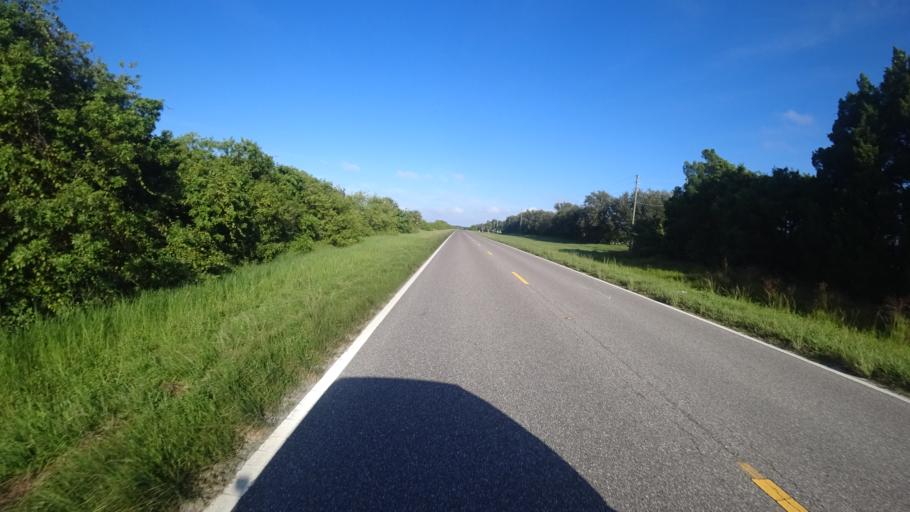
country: US
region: Florida
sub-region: Hillsborough County
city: Sun City Center
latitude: 27.5429
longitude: -82.3516
